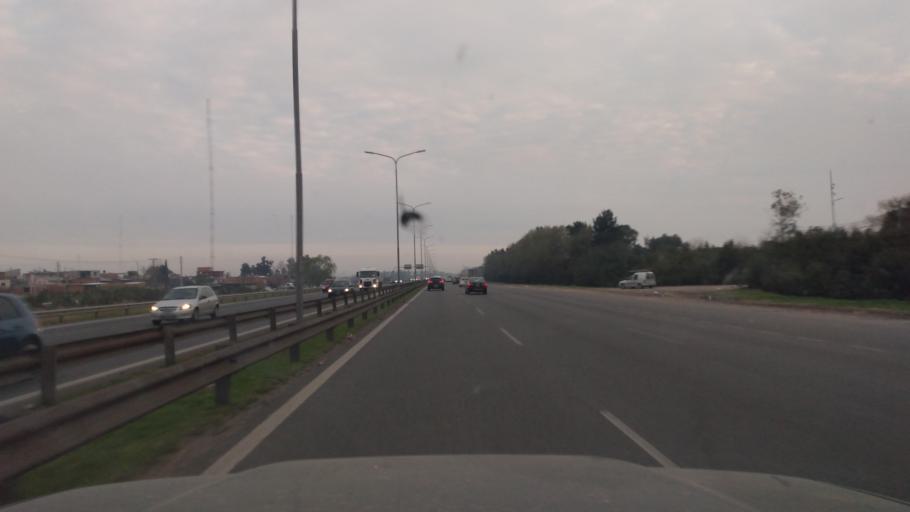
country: AR
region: Buenos Aires
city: Hurlingham
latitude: -34.5359
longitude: -58.5979
